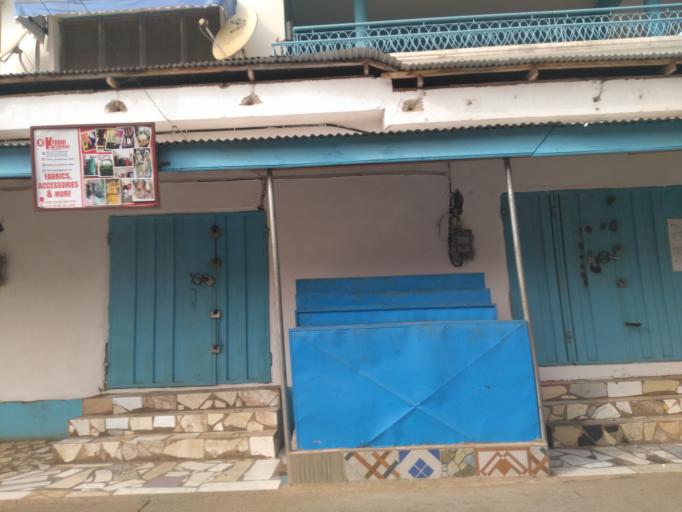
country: GH
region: Ashanti
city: Kumasi
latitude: 6.6952
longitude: -1.6242
